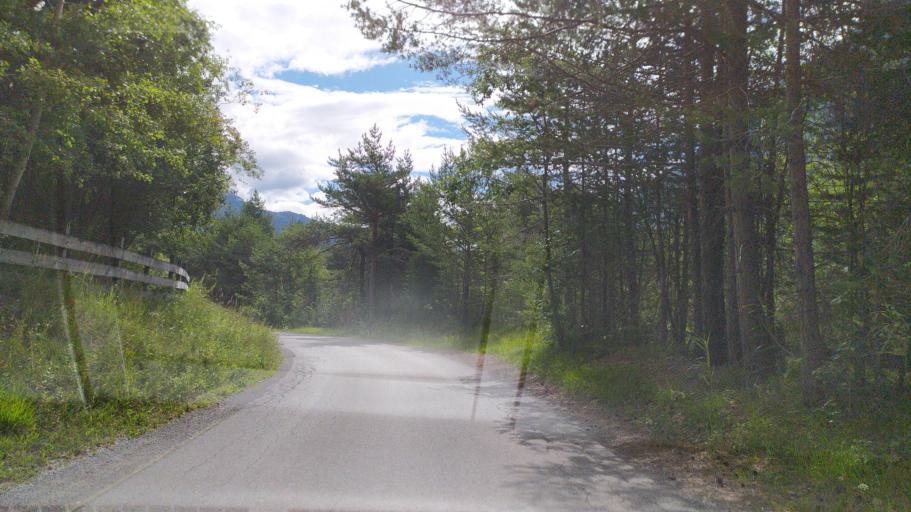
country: AT
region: Tyrol
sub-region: Politischer Bezirk Lienz
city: Lavant
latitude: 46.7901
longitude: 12.8678
